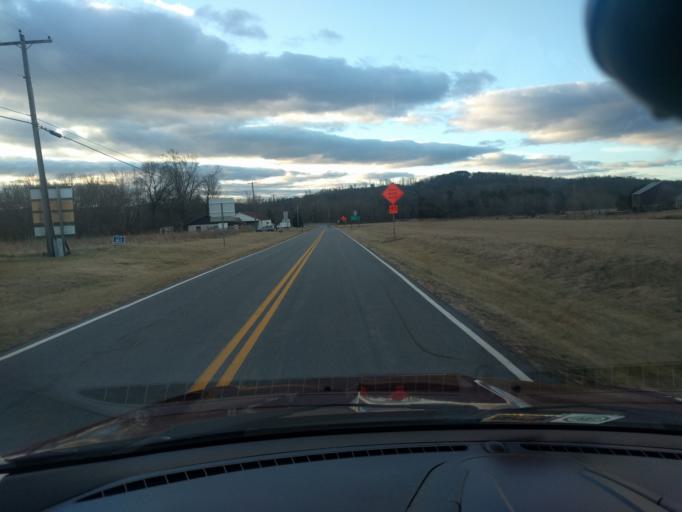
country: US
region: Virginia
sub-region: City of Bedford
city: Bedford
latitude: 37.3956
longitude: -79.5559
